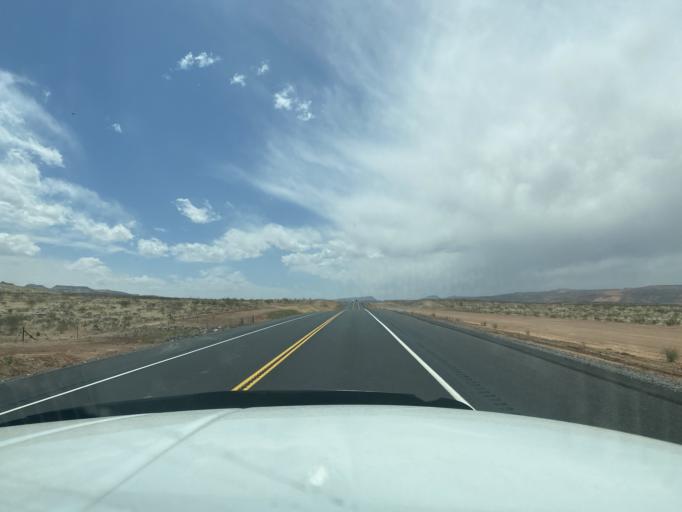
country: US
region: Utah
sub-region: Washington County
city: Hurricane
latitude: 37.1590
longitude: -113.3458
